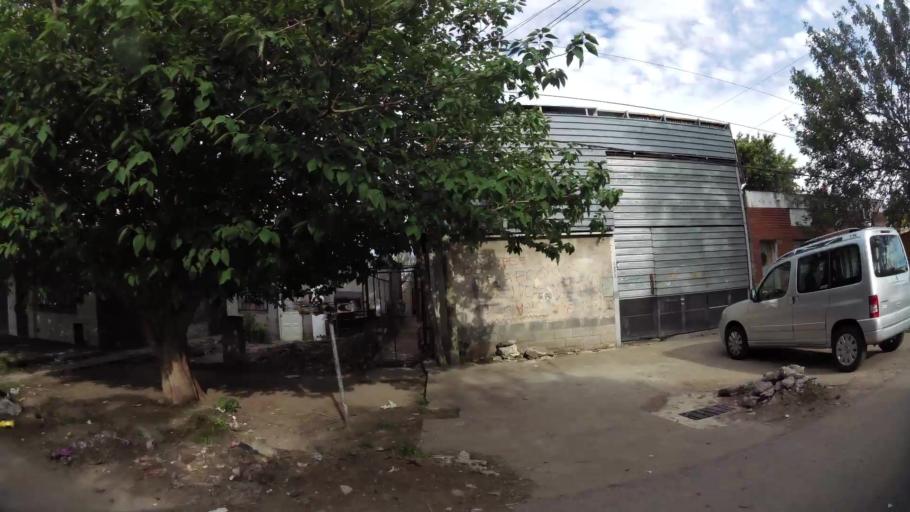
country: AR
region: Santa Fe
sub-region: Departamento de Rosario
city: Rosario
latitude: -32.9756
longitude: -60.6841
